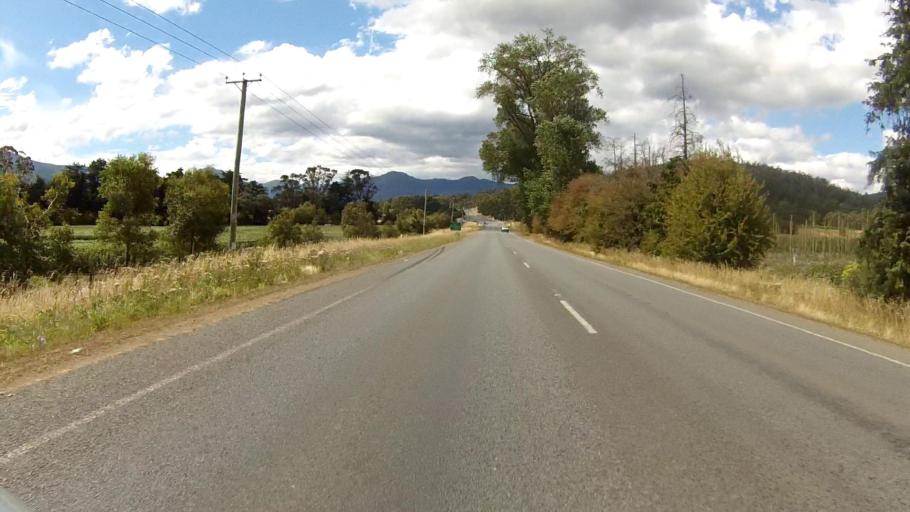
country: AU
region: Tasmania
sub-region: Huon Valley
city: Huonville
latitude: -42.9846
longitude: 147.0922
